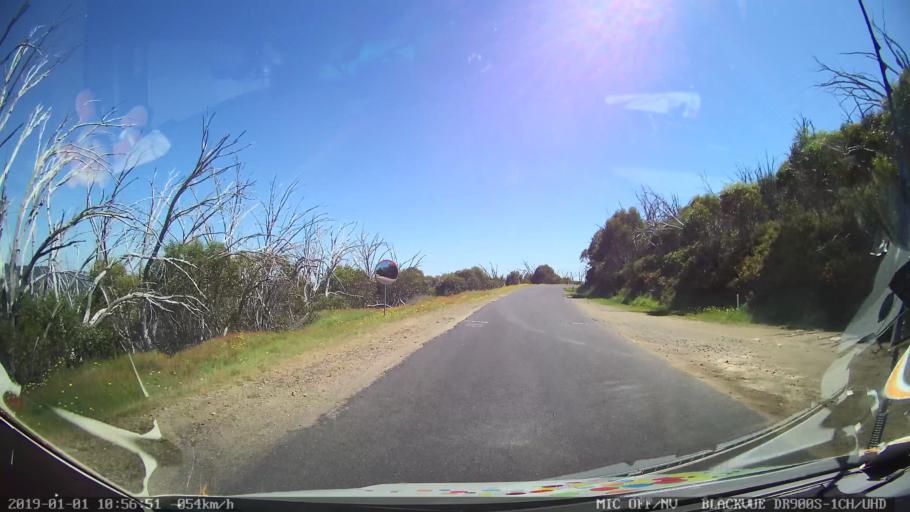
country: AU
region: New South Wales
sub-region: Snowy River
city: Jindabyne
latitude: -36.0013
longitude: 148.3940
